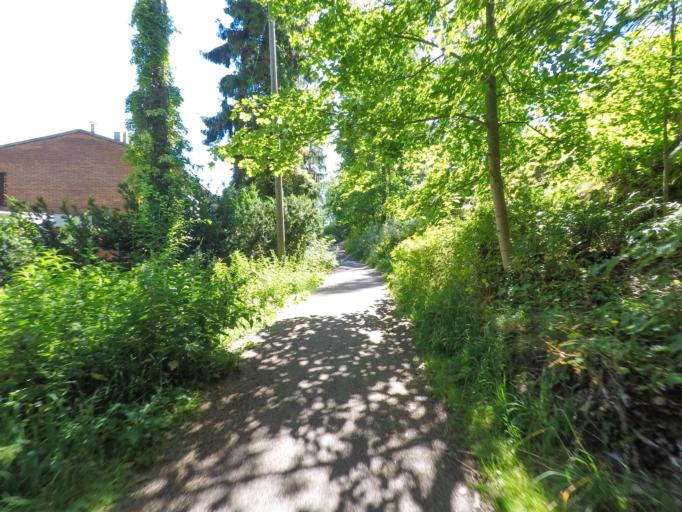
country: FI
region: Uusimaa
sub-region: Helsinki
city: Vantaa
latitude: 60.1859
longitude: 25.0606
